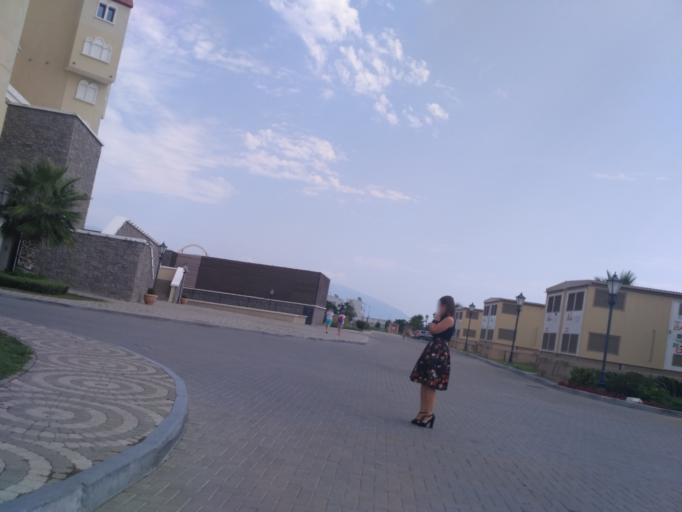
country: RU
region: Krasnodarskiy
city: Adler
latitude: 43.4030
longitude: 39.9629
